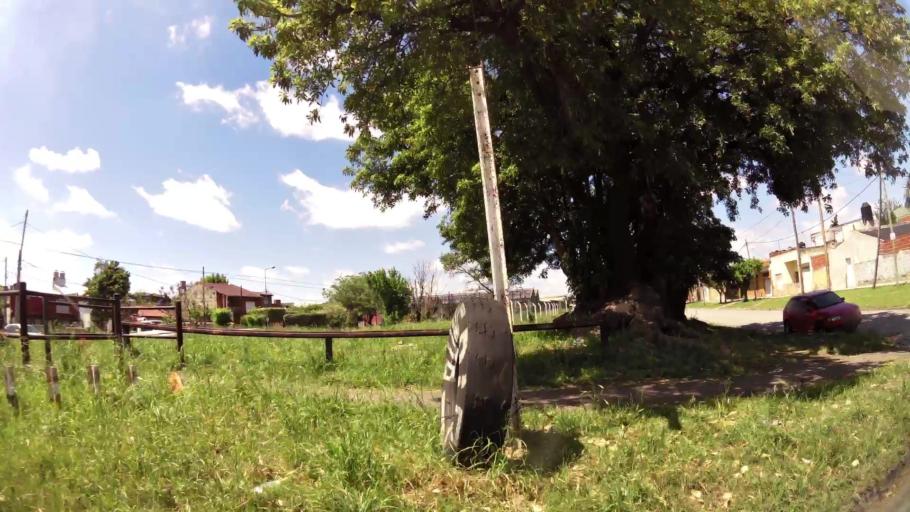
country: AR
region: Buenos Aires
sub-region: Partido de Lanus
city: Lanus
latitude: -34.6911
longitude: -58.4272
